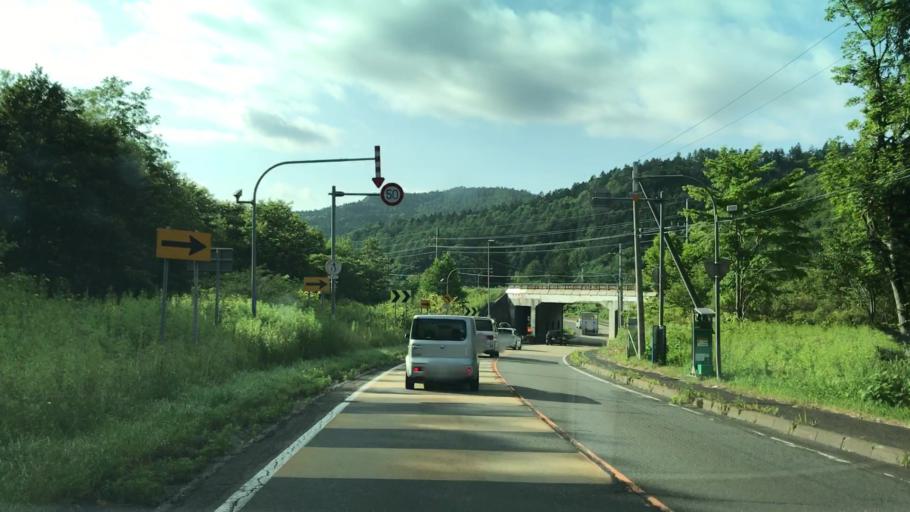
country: JP
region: Hokkaido
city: Iwamizawa
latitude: 42.9300
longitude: 142.0950
